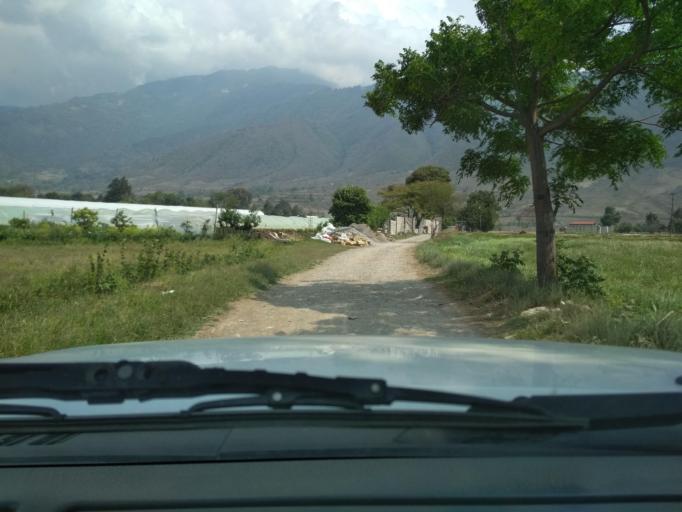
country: MX
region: Veracruz
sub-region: Acultzingo
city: Acatla
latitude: 18.7580
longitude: -97.2296
